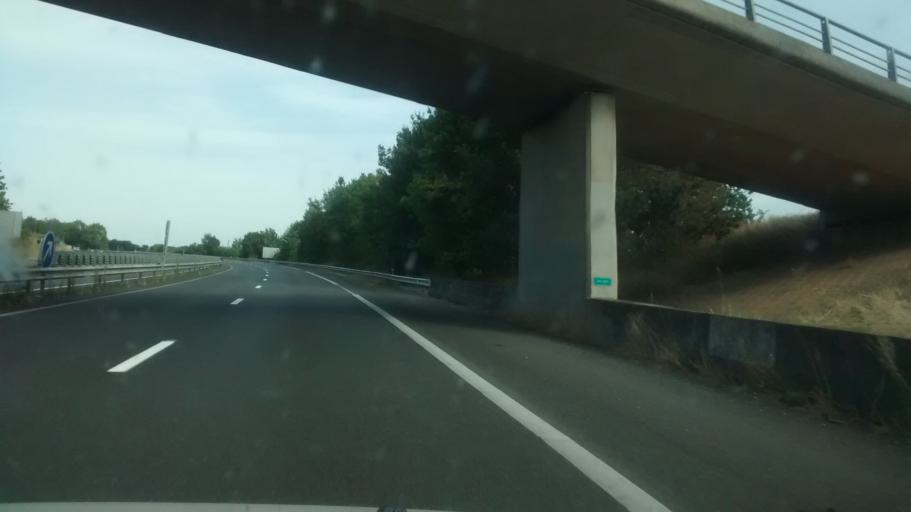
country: FR
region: Aquitaine
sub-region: Departement du Lot-et-Garonne
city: Boe
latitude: 44.1543
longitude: 0.6192
